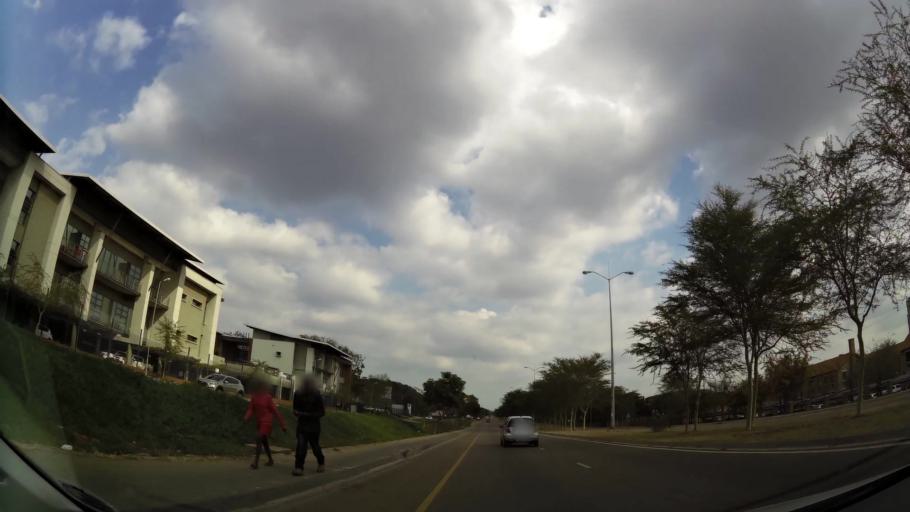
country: ZA
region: Gauteng
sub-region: City of Tshwane Metropolitan Municipality
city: Pretoria
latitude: -25.7662
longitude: 28.3082
